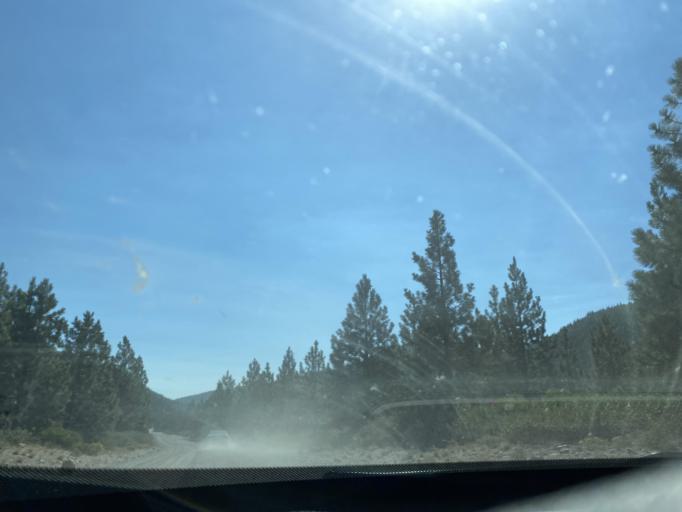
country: US
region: Oregon
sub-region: Deschutes County
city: Sunriver
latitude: 44.0345
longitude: -121.5354
